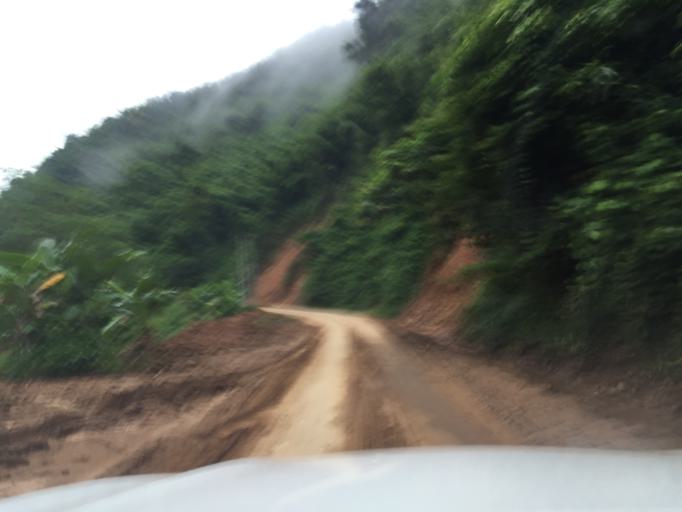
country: LA
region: Phongsali
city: Khoa
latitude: 21.0769
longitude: 102.3775
